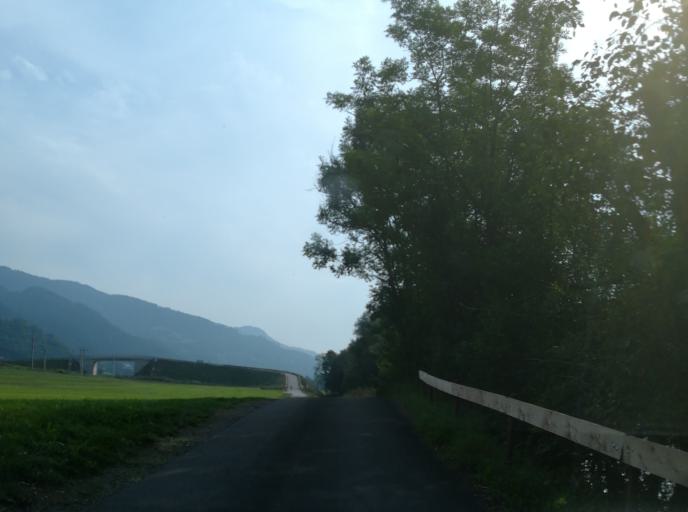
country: AT
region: Styria
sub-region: Politischer Bezirk Murtal
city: Sankt Georgen ob Judenburg
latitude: 47.2115
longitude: 14.4593
